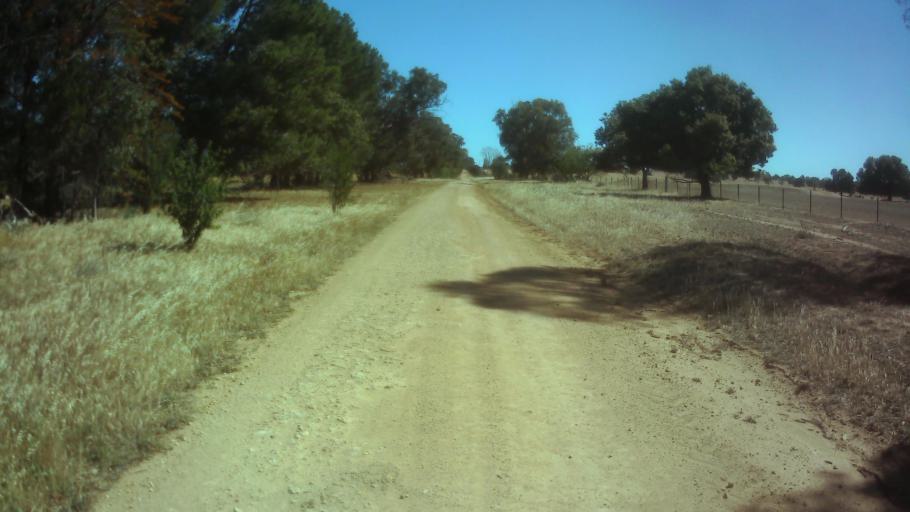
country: AU
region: New South Wales
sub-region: Weddin
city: Grenfell
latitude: -33.9897
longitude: 148.3403
